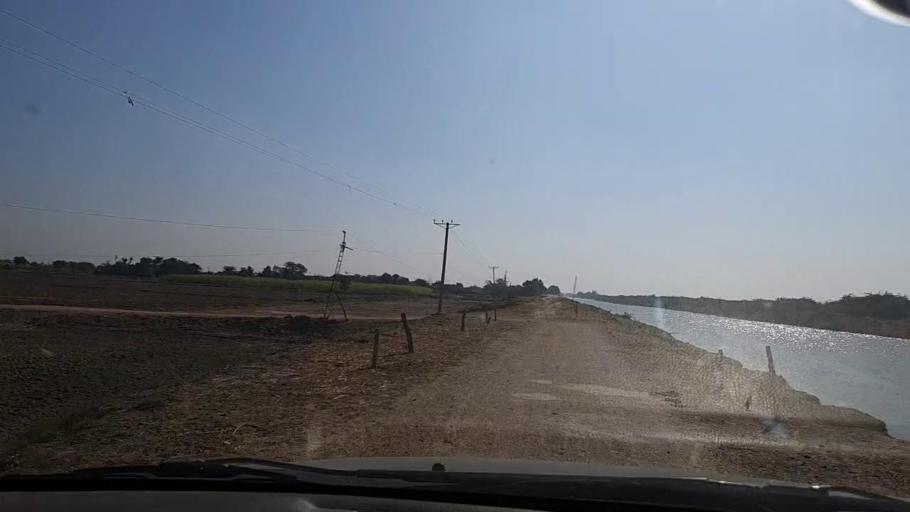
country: PK
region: Sindh
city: Thatta
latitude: 24.6009
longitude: 68.0504
